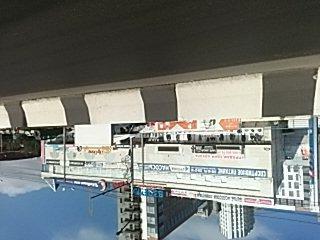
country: RU
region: Krasnoyarskiy
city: Krasnoyarsk
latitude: 56.0344
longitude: 92.9255
